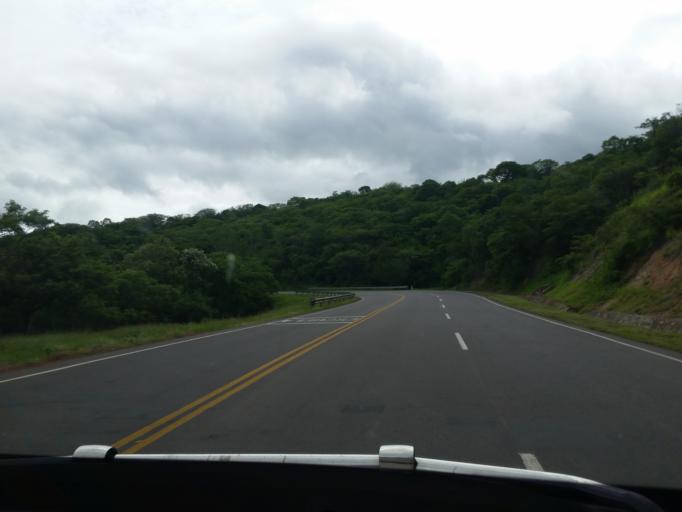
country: NI
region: Matagalpa
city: Matagalpa
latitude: 12.8850
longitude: -86.0533
